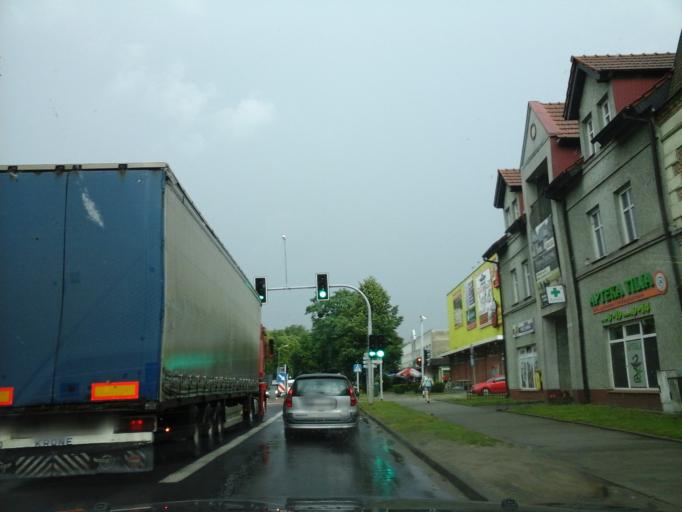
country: PL
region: Greater Poland Voivodeship
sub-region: Powiat miedzychodzki
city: Miedzychod
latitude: 52.6013
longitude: 15.8893
